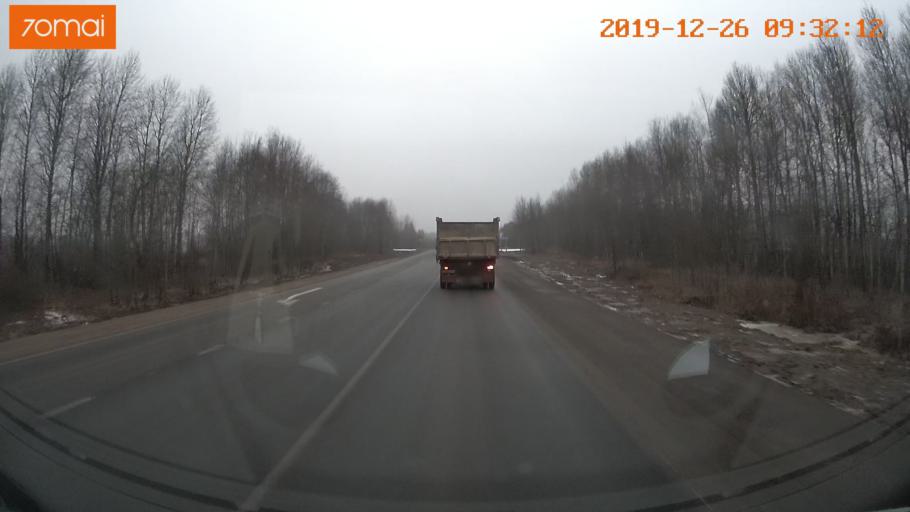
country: RU
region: Vologda
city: Gryazovets
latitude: 59.0755
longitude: 40.1196
